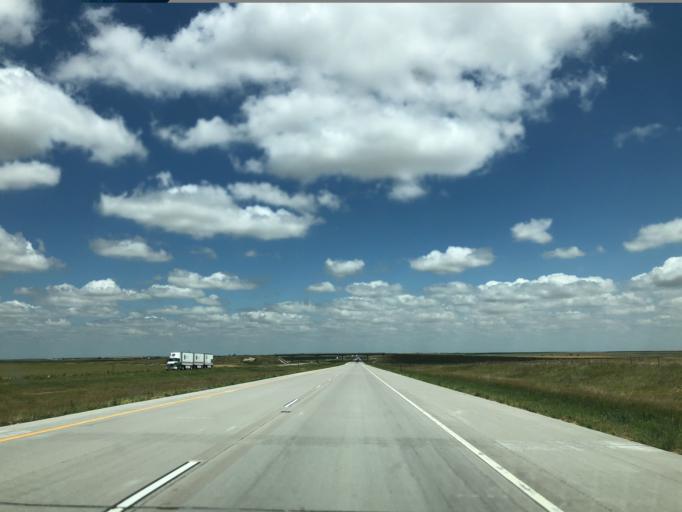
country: US
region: Colorado
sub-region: Kit Carson County
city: Burlington
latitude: 39.2940
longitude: -102.7859
